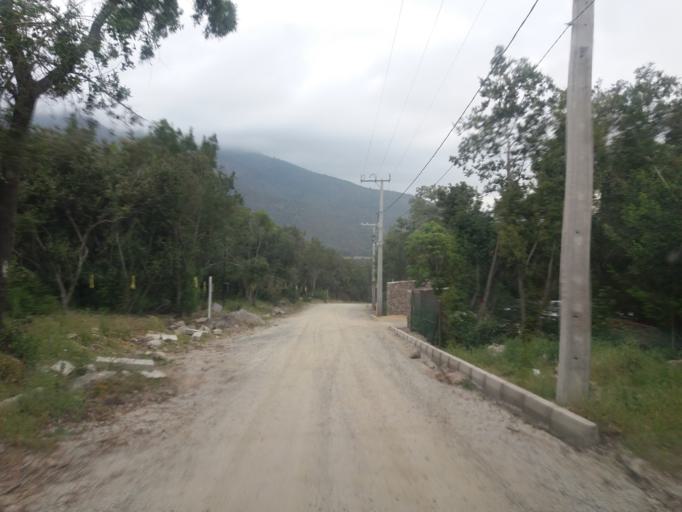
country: CL
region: Valparaiso
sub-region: Provincia de Marga Marga
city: Limache
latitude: -33.0240
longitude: -71.1271
